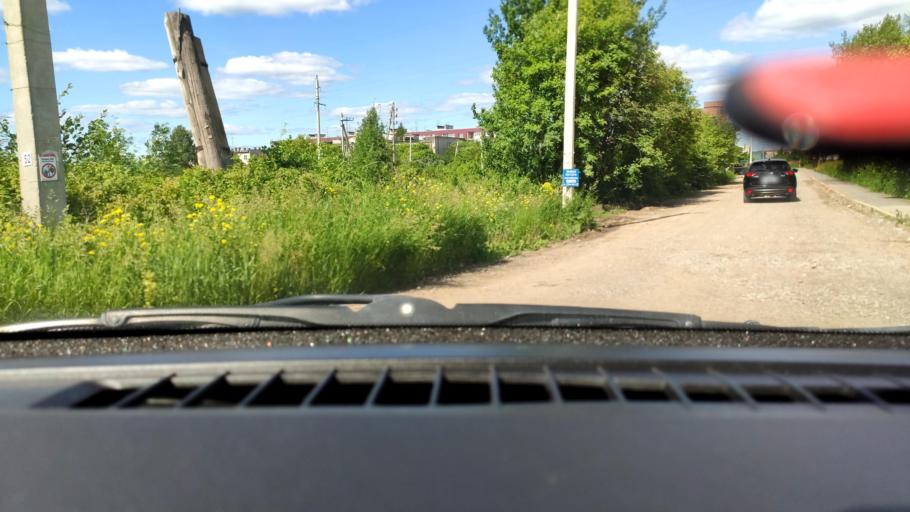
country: RU
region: Perm
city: Kultayevo
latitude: 57.8902
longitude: 55.9211
